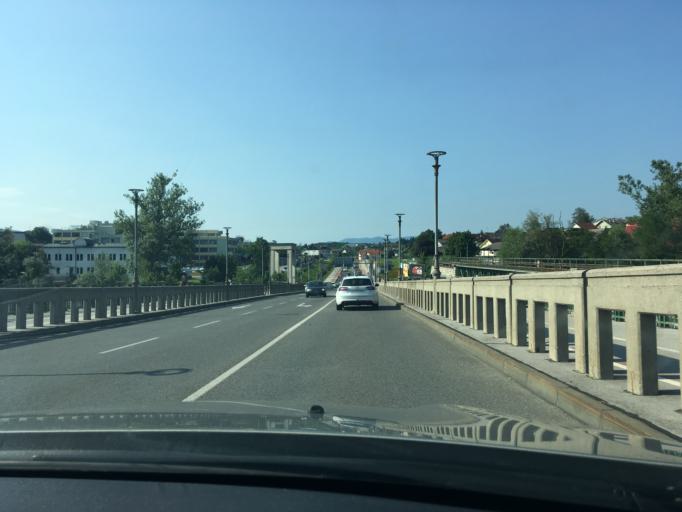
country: SI
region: Novo Mesto
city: Novo Mesto
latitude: 45.8037
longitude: 15.1622
